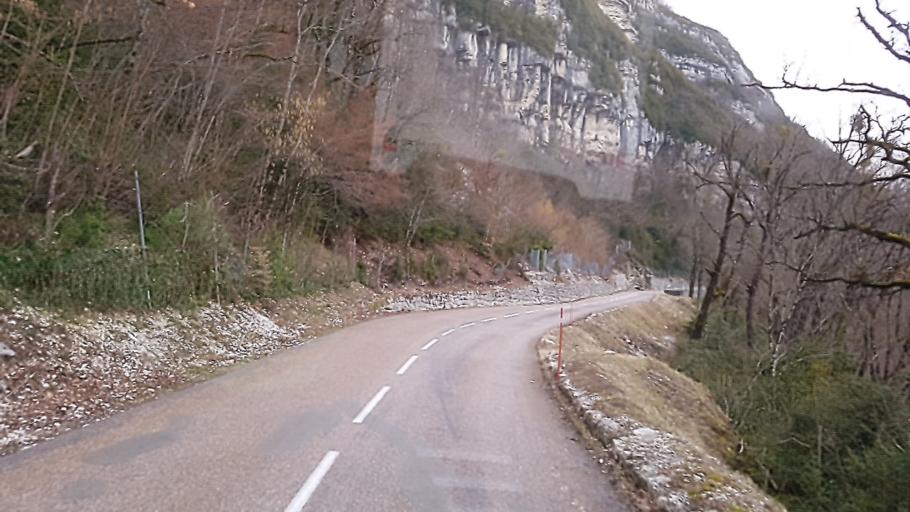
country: FR
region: Franche-Comte
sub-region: Departement du Jura
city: Saint-Claude
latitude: 46.3634
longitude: 5.8924
